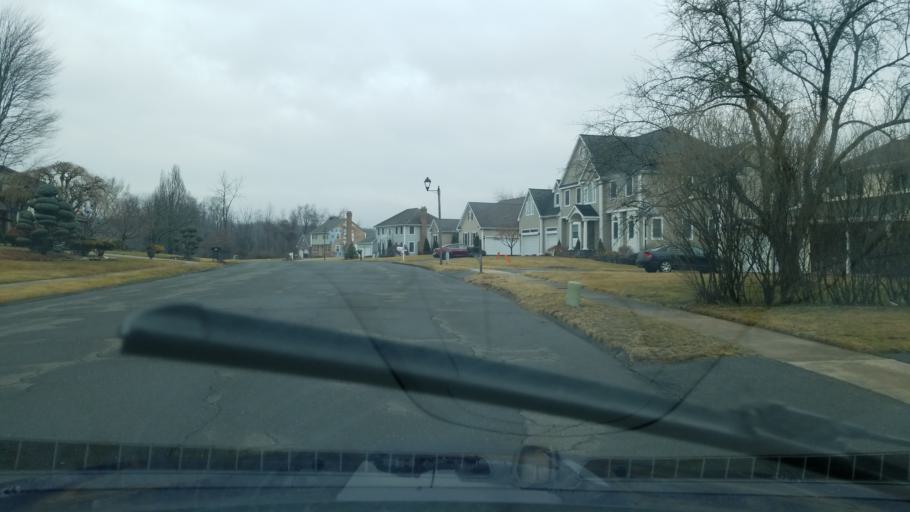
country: US
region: Connecticut
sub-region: Hartford County
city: Newington
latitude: 41.6741
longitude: -72.6959
